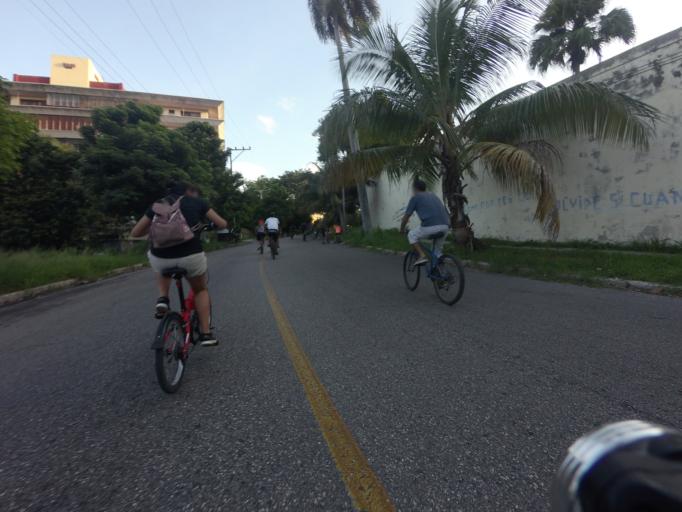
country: CU
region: La Habana
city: Havana
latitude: 23.1239
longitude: -82.4124
